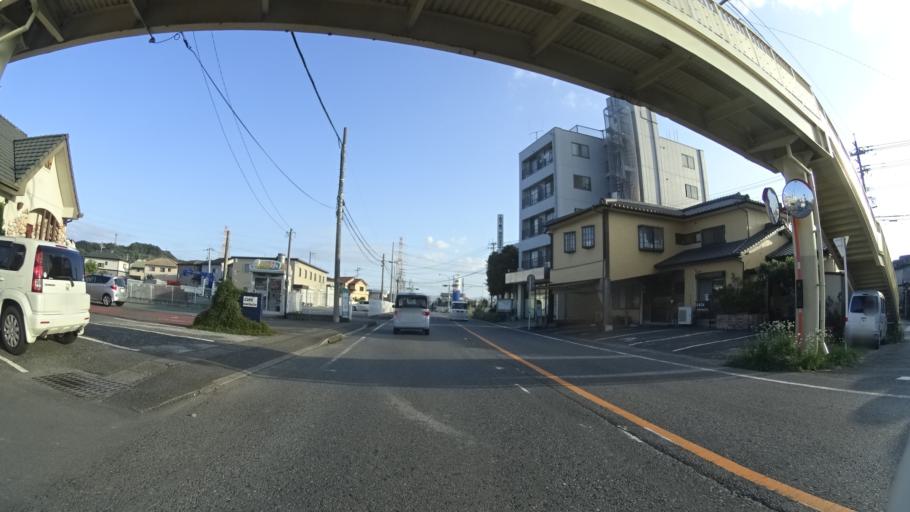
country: JP
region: Kumamoto
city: Uto
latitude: 32.6691
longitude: 130.6703
